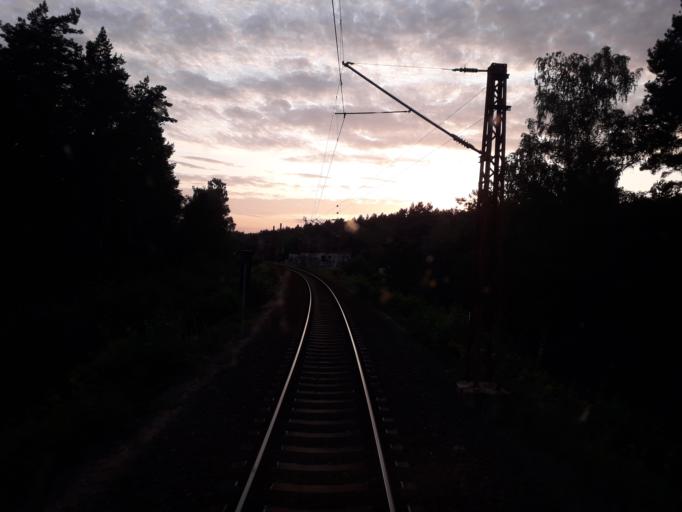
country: DE
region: Brandenburg
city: Hennigsdorf
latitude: 52.6586
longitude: 13.1974
